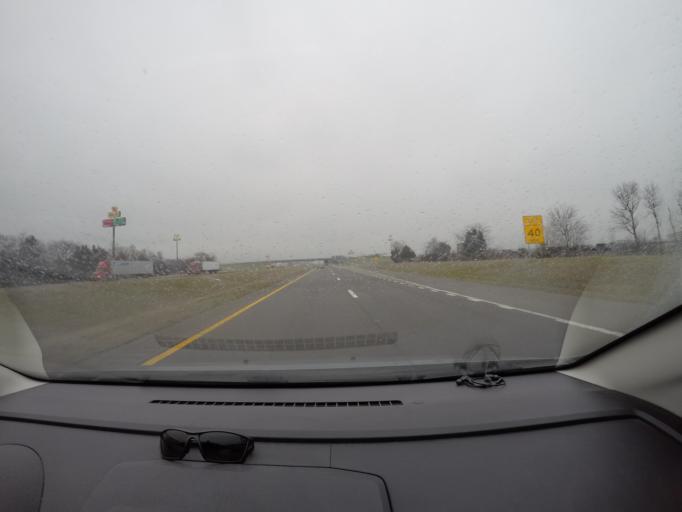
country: US
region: Tennessee
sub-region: Rutherford County
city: Plainview
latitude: 35.7249
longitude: -86.3231
